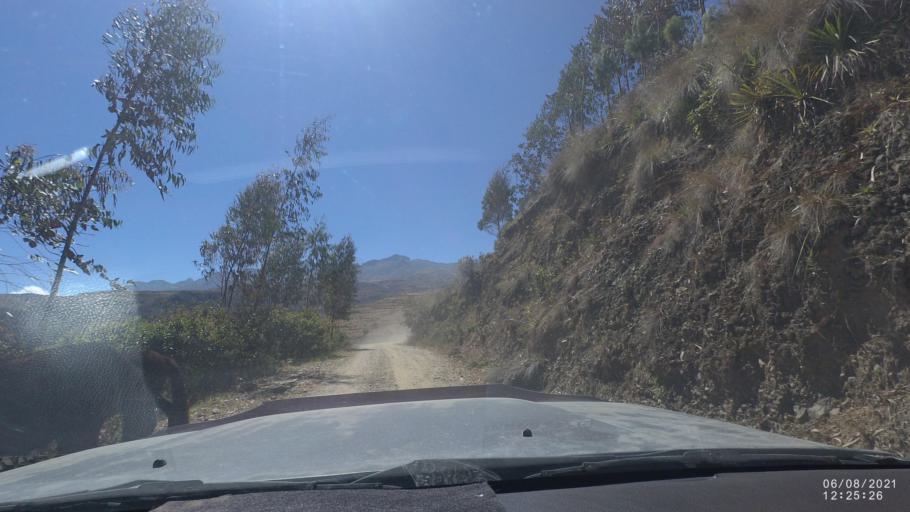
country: BO
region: Cochabamba
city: Colchani
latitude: -16.7947
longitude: -66.6570
